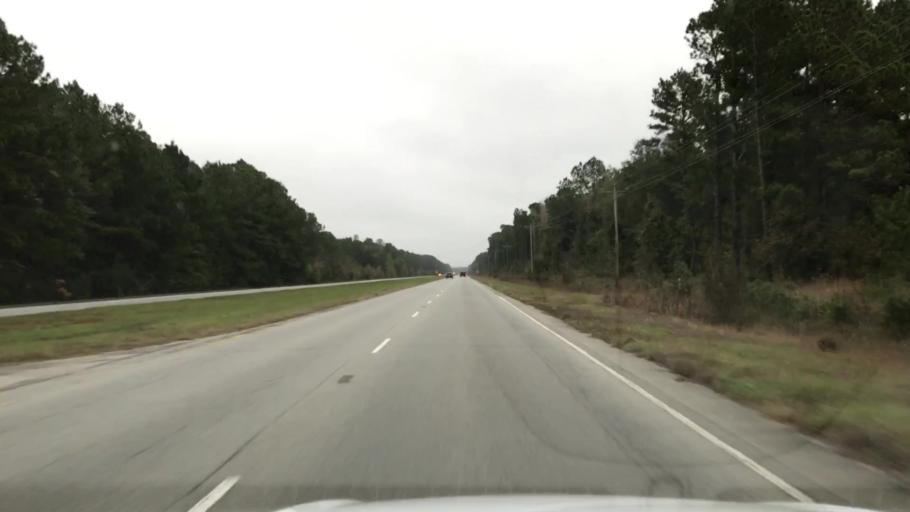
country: US
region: South Carolina
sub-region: Charleston County
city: Awendaw
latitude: 33.0056
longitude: -79.6414
